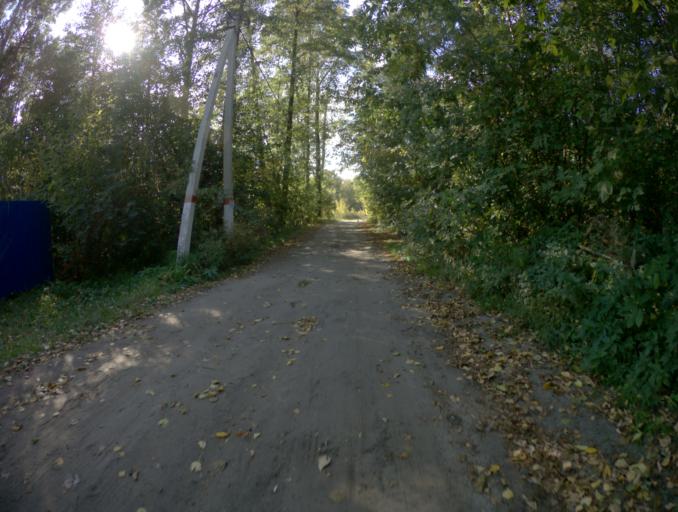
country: RU
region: Moskovskaya
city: Kerva
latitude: 55.6099
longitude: 39.5706
